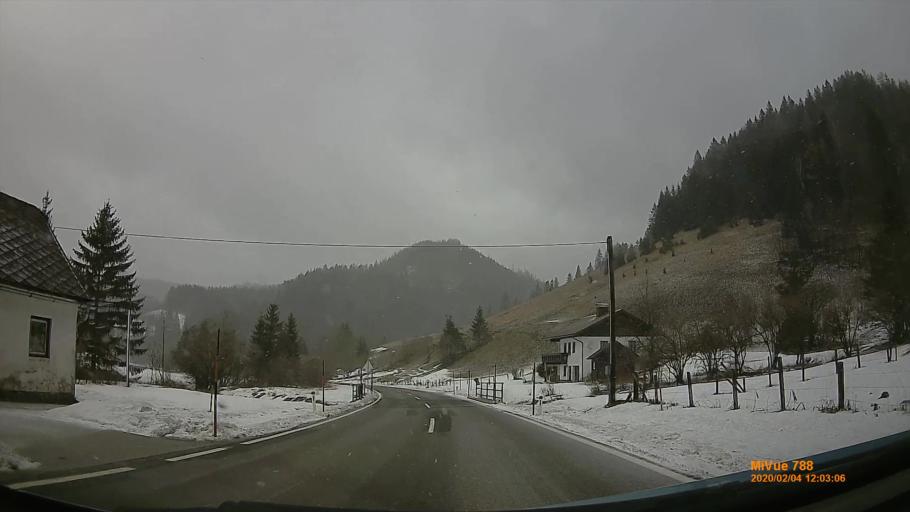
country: AT
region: Styria
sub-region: Politischer Bezirk Bruck-Muerzzuschlag
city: Muerzsteg
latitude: 47.7725
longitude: 15.4558
